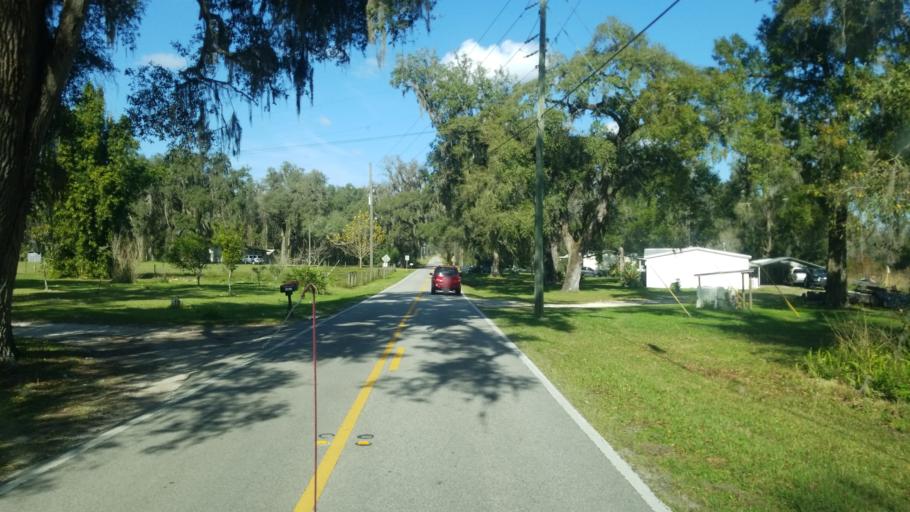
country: US
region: Florida
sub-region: Hernando County
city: North Brooksville
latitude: 28.5952
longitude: -82.3760
